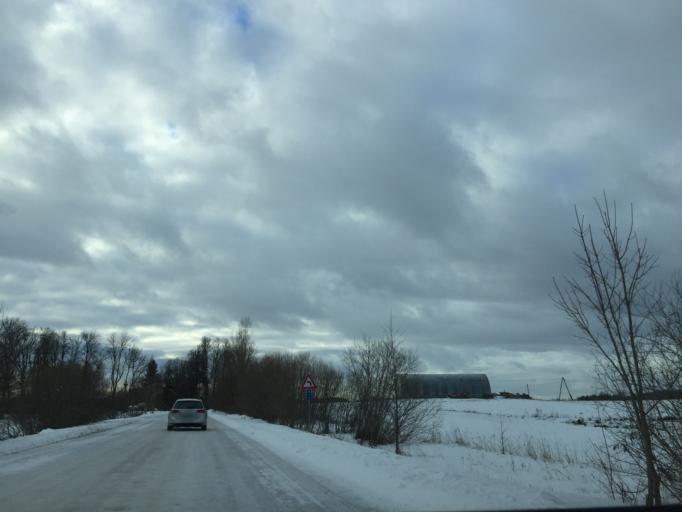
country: LV
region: Lielvarde
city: Lielvarde
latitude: 56.6121
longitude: 24.7643
